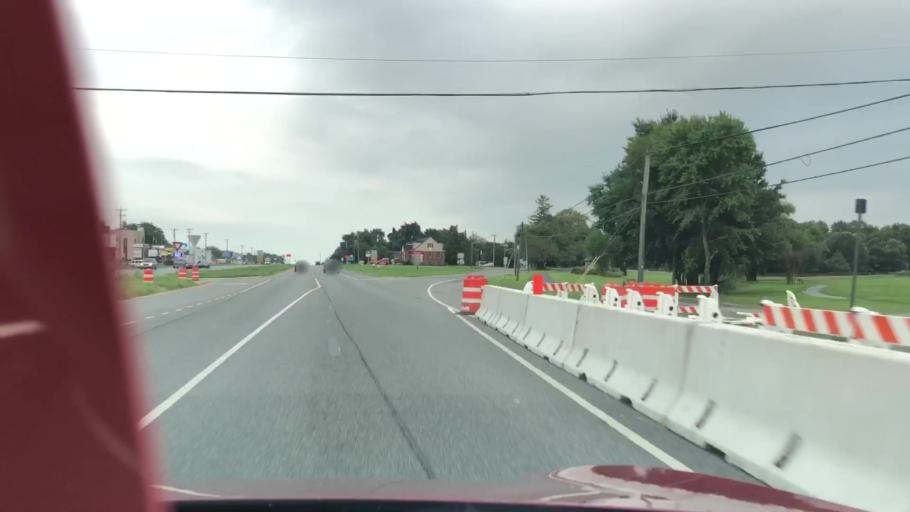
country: US
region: Delaware
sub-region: Kent County
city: Highland Acres
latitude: 39.1222
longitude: -75.5303
